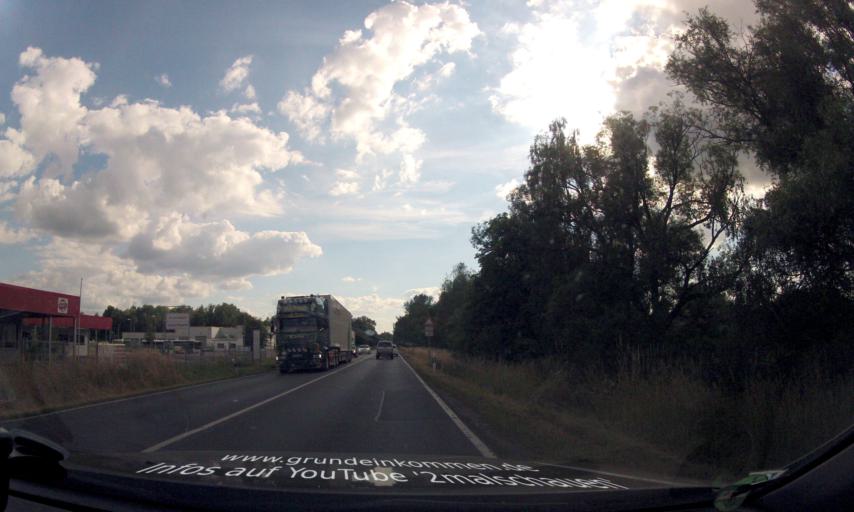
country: DE
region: Saxony
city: Bennewitz
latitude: 51.3615
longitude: 12.6941
